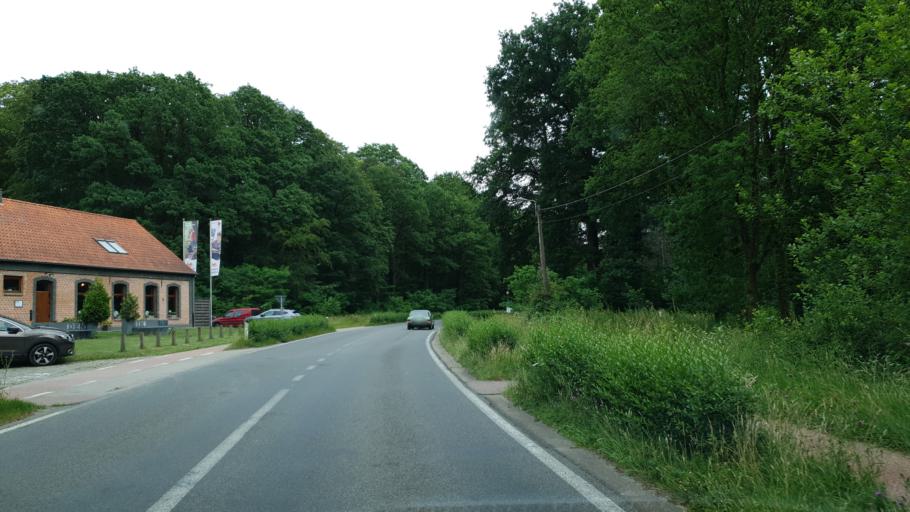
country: BE
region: Flanders
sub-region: Provincie Vlaams-Brabant
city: Scherpenheuvel-Zichem
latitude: 51.0372
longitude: 4.9709
